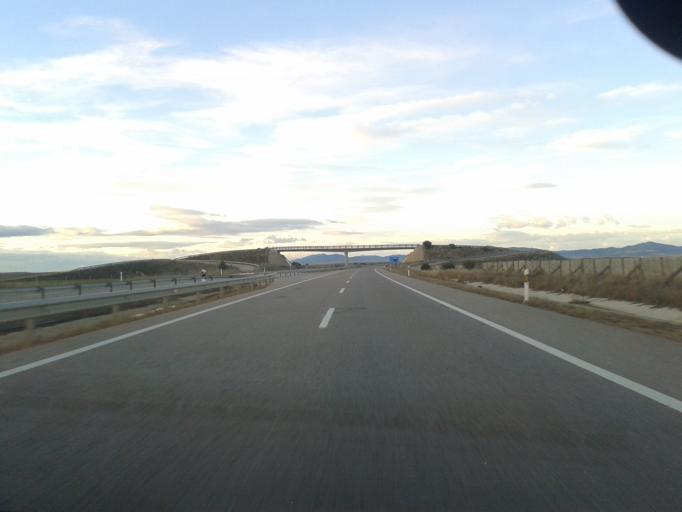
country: ES
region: Aragon
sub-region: Provincia de Zaragoza
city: Lechon
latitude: 41.0722
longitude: -1.2861
